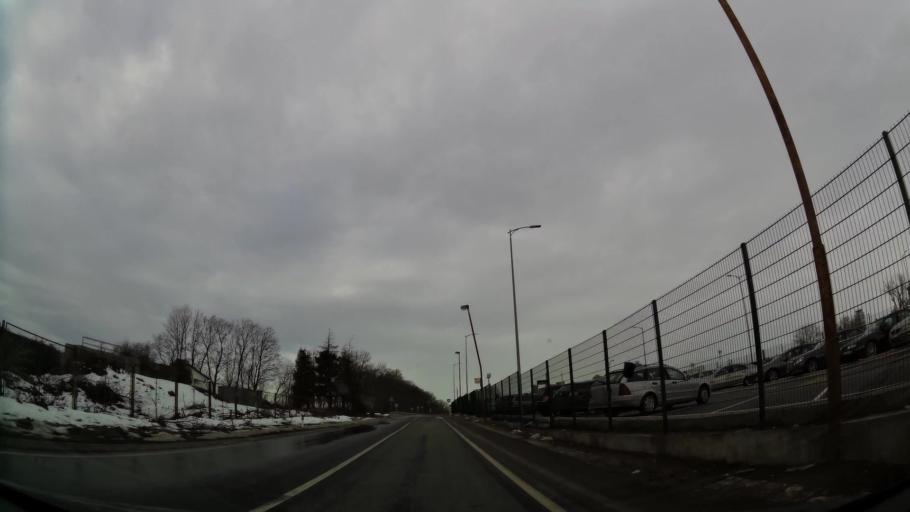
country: RS
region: Central Serbia
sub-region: Belgrade
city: Surcin
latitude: 44.8136
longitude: 20.2917
